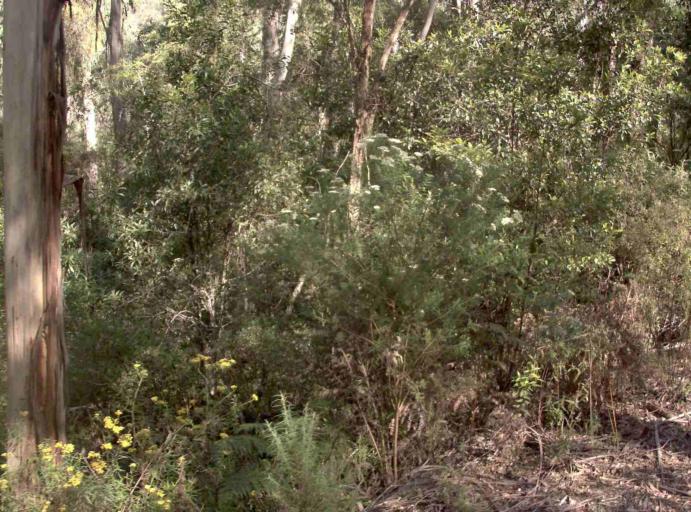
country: AU
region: Victoria
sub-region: East Gippsland
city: Lakes Entrance
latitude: -37.4683
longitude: 148.5610
